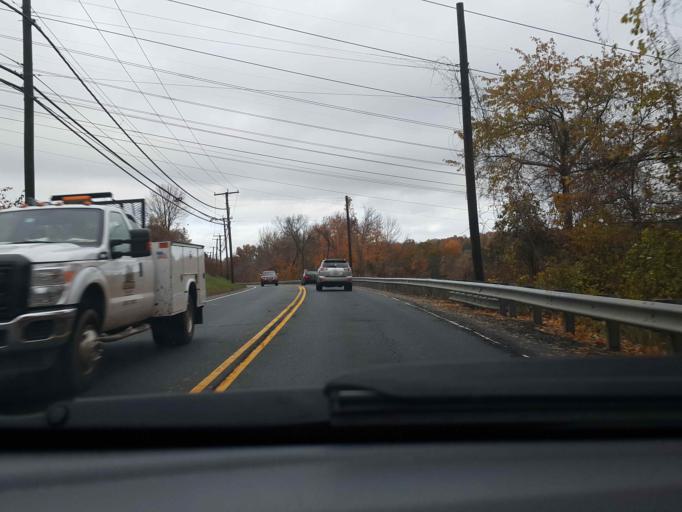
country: US
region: Connecticut
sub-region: Middlesex County
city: Durham
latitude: 41.5100
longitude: -72.6702
